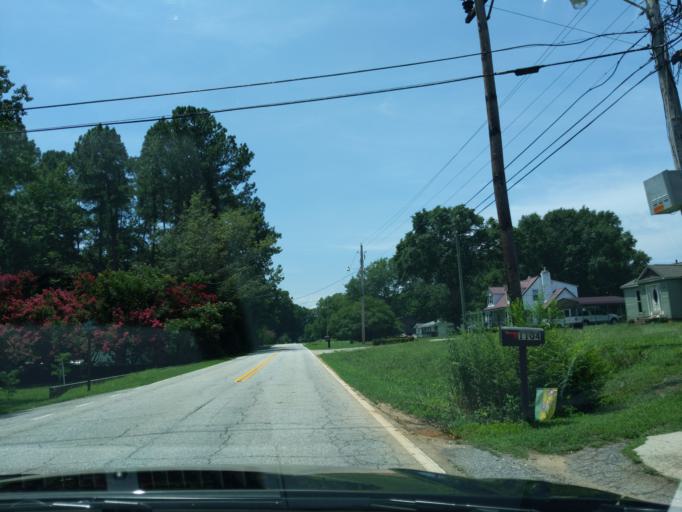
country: US
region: South Carolina
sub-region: Laurens County
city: Laurens
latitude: 34.4847
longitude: -82.0246
